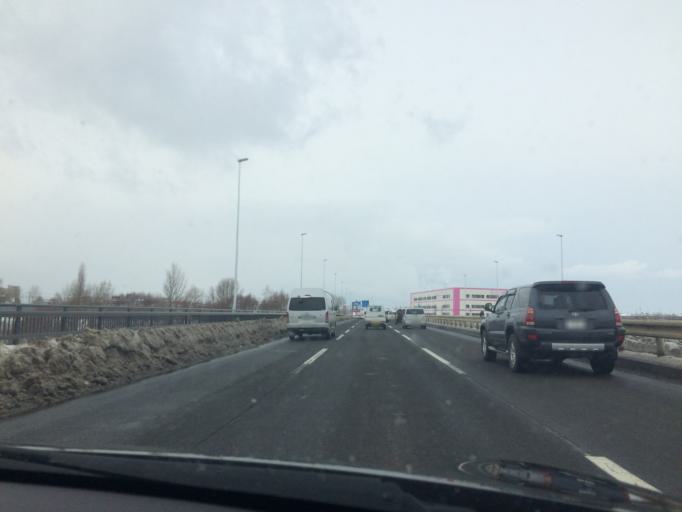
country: JP
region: Hokkaido
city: Sapporo
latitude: 43.0738
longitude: 141.4050
